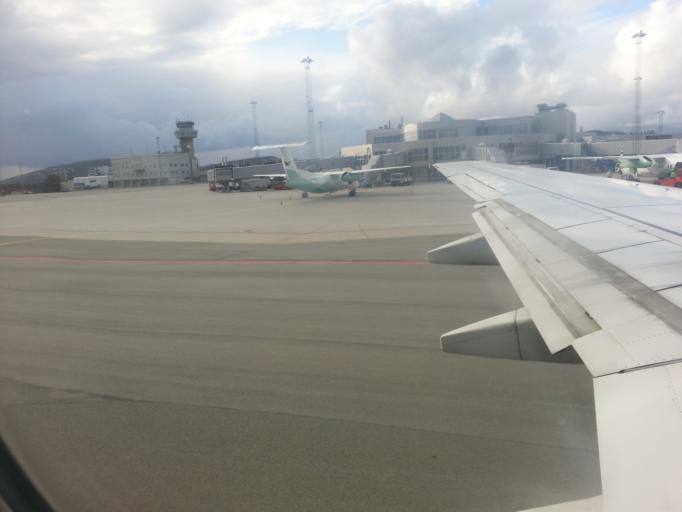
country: NO
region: Nordland
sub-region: Bodo
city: Bodo
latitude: 67.2703
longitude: 14.3696
